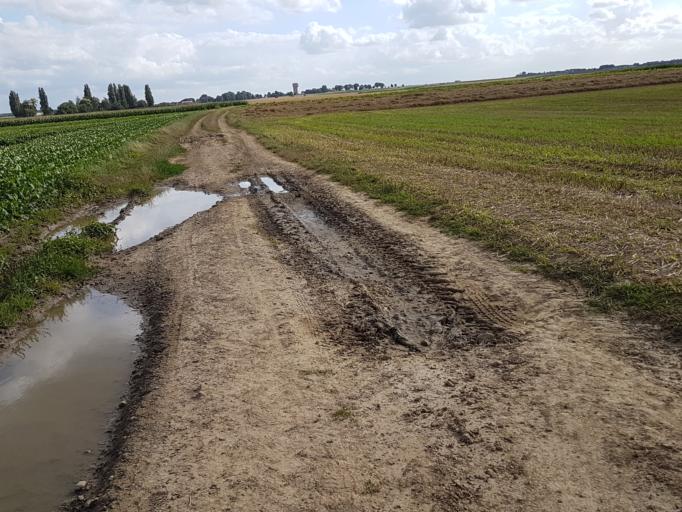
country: BE
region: Flanders
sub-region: Provincie Vlaams-Brabant
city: Kortenberg
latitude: 50.9111
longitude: 4.5409
